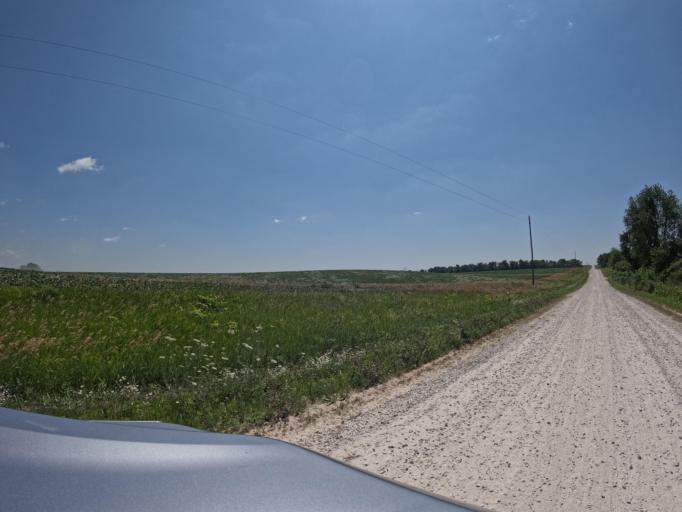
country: US
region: Iowa
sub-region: Keokuk County
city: Sigourney
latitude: 41.2876
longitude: -92.2382
